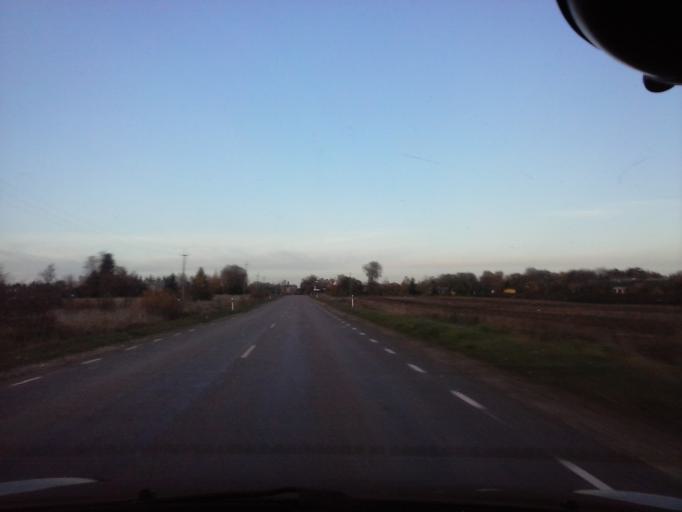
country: EE
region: Harju
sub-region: Nissi vald
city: Turba
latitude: 58.9139
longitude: 24.1539
